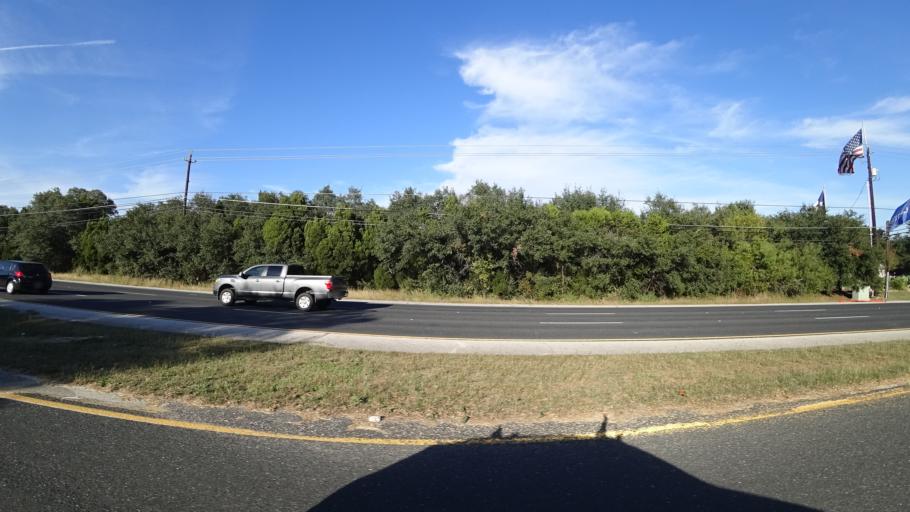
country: US
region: Texas
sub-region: Travis County
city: Barton Creek
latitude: 30.2468
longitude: -97.8473
